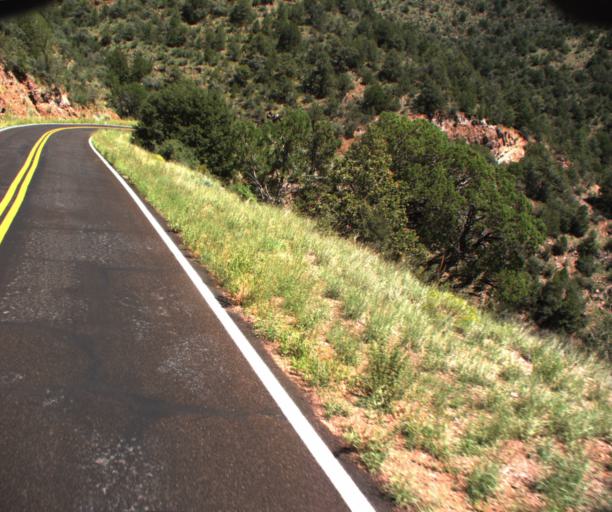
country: US
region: Arizona
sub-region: Greenlee County
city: Morenci
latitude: 33.4132
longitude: -109.3637
